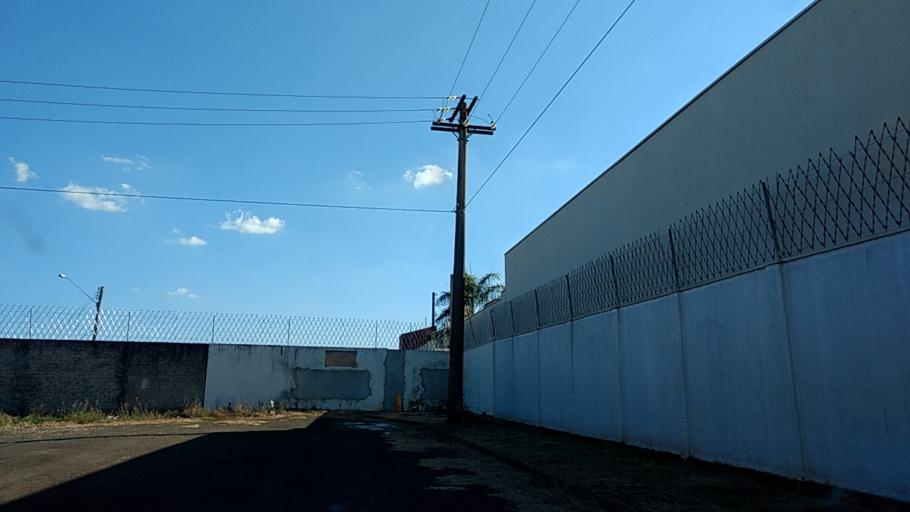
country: BR
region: Sao Paulo
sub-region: Botucatu
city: Botucatu
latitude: -22.8546
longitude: -48.4373
